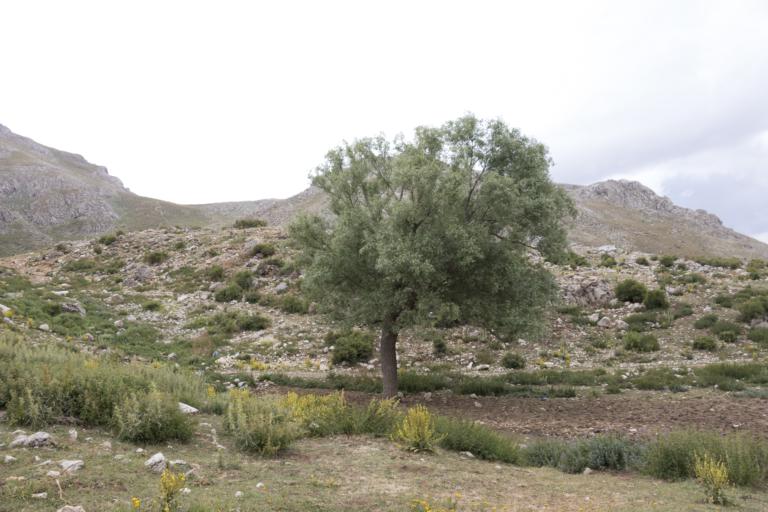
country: TR
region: Kayseri
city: Toklar
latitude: 38.4301
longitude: 36.1646
